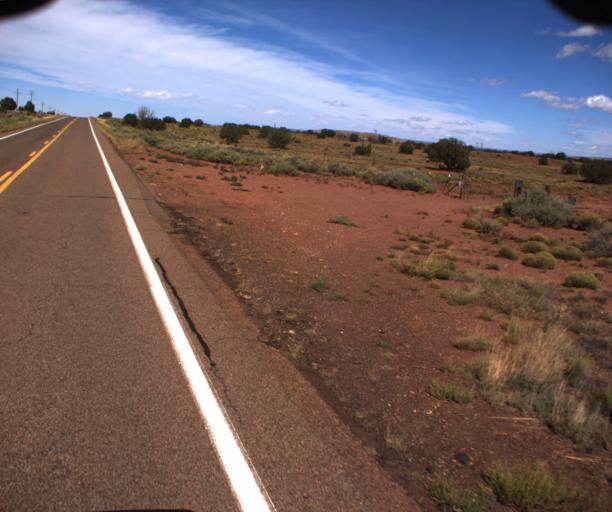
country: US
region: Arizona
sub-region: Apache County
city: Saint Johns
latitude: 34.5259
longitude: -109.6204
